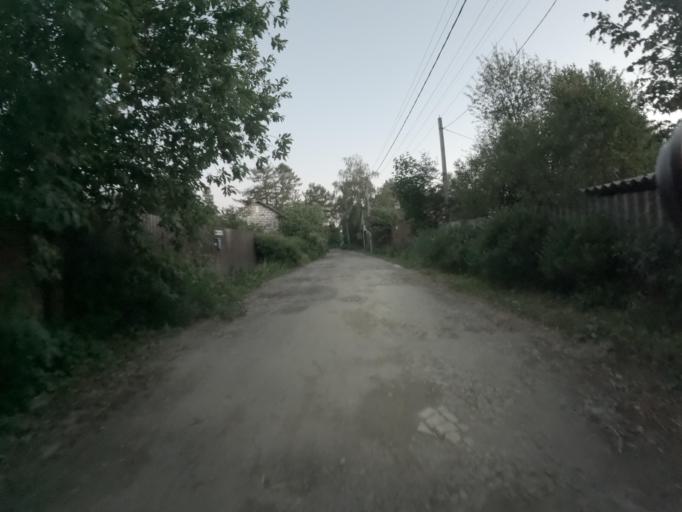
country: RU
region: Leningrad
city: Vsevolozhsk
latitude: 60.0123
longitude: 30.6094
